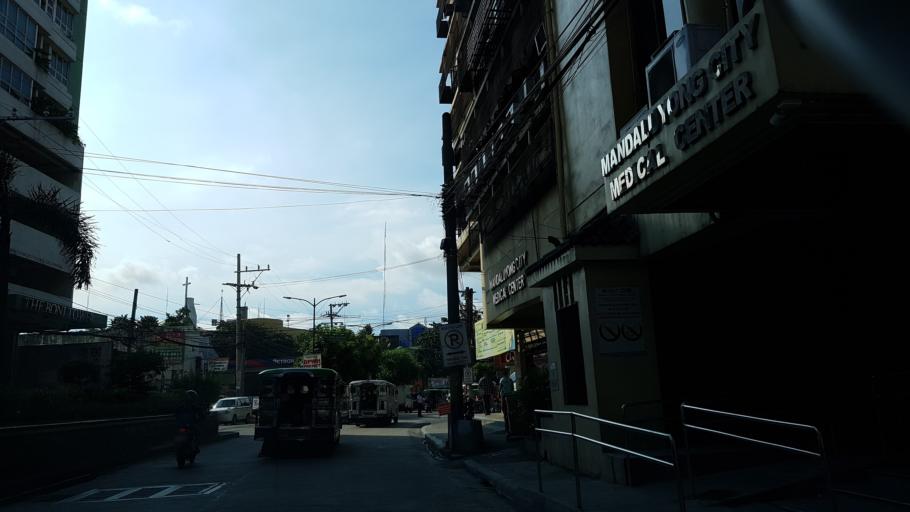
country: PH
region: Metro Manila
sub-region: Mandaluyong
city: Mandaluyong City
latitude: 14.5760
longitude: 121.0355
